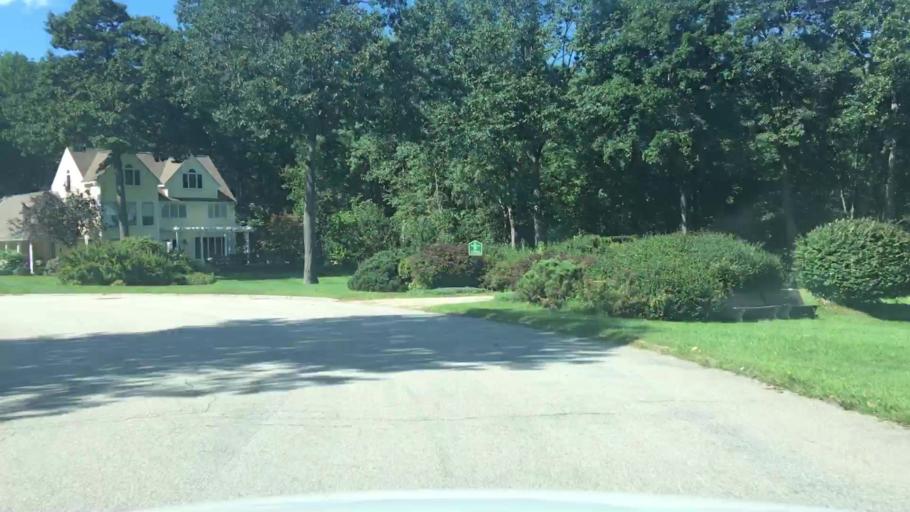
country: US
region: Maine
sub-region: York County
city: Eliot
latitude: 43.1707
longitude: -70.8318
